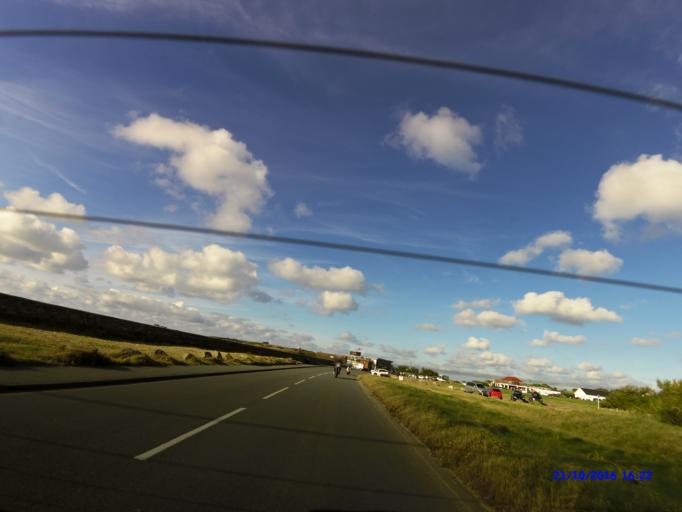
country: GG
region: St Peter Port
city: Saint Peter Port
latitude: 49.4696
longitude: -2.6061
